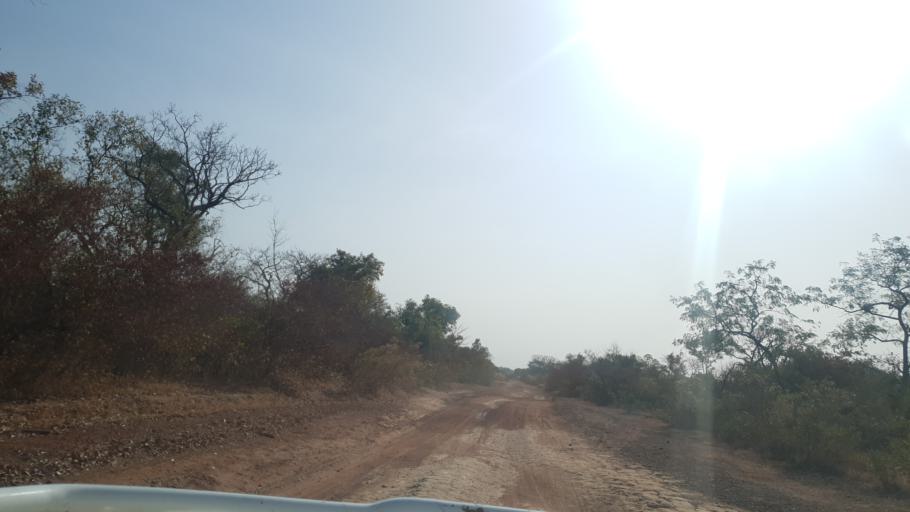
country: ML
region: Koulikoro
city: Dioila
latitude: 12.7105
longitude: -6.7862
